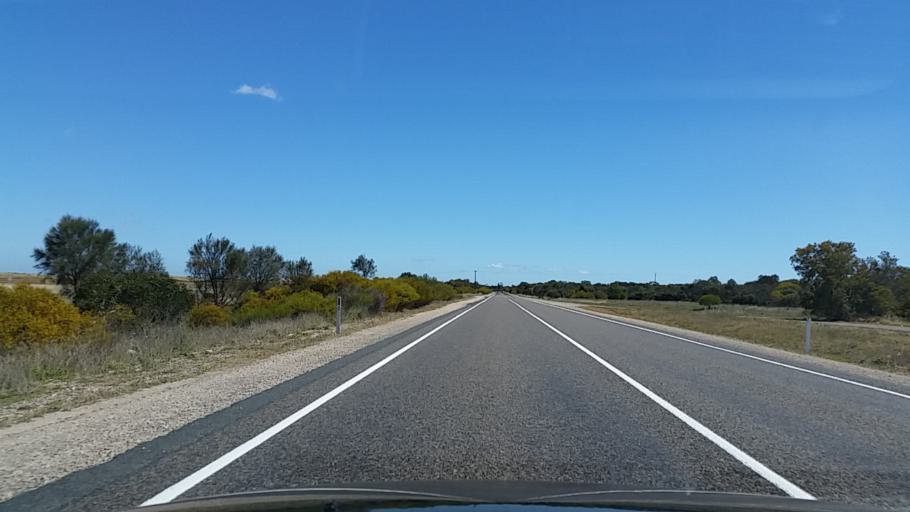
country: AU
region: South Australia
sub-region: Murray Bridge
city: Tailem Bend
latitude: -35.2901
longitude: 139.4461
